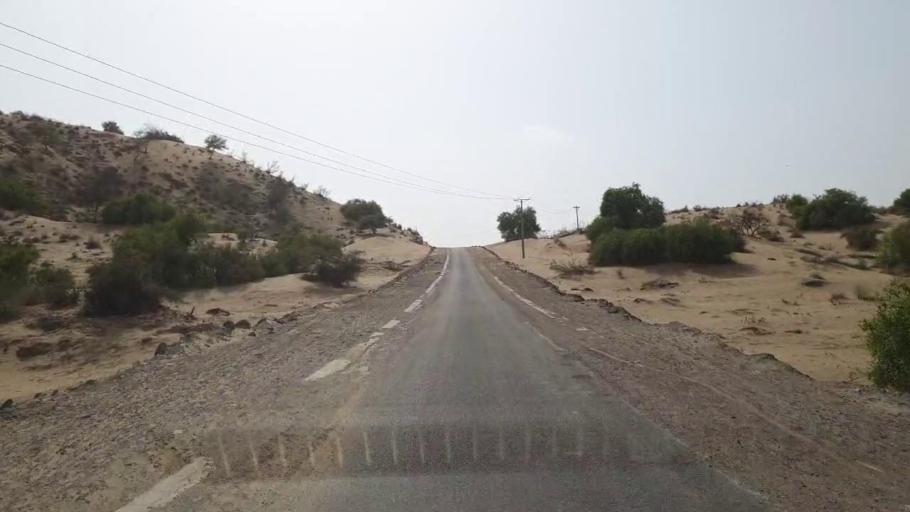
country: PK
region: Sindh
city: Mithi
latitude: 24.6213
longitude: 69.9131
